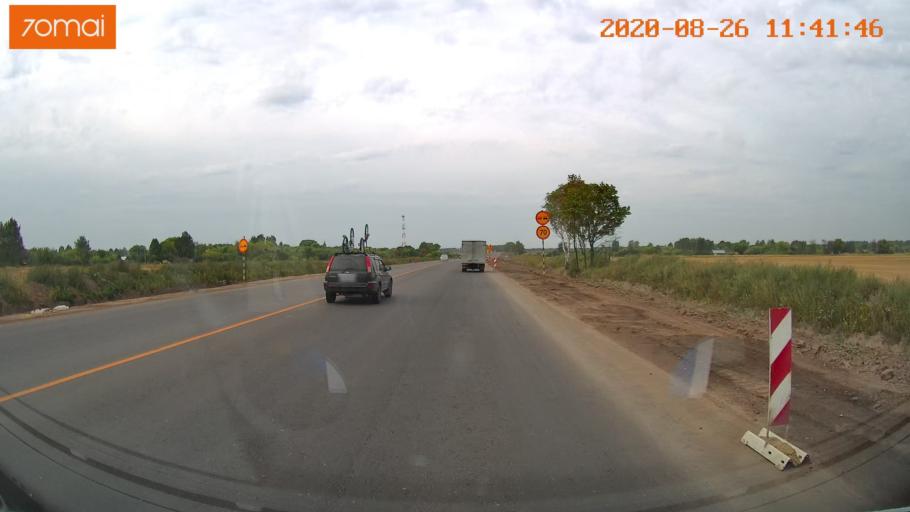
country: RU
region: Rjazan
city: Shilovo
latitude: 54.2958
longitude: 40.7047
